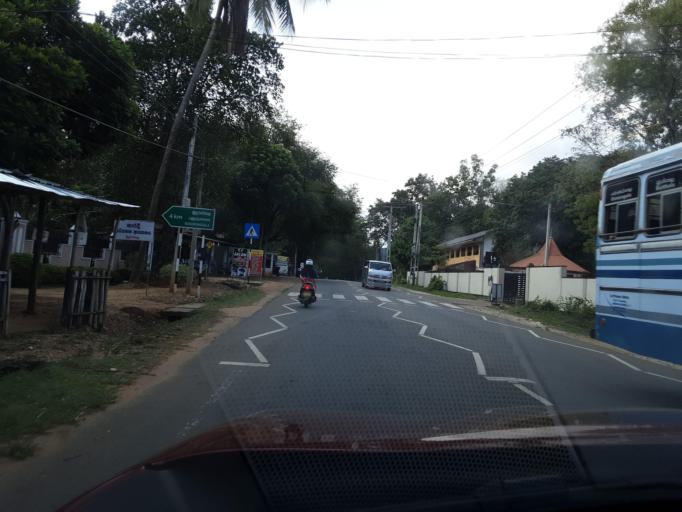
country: LK
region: Uva
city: Haputale
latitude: 6.6896
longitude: 81.1075
